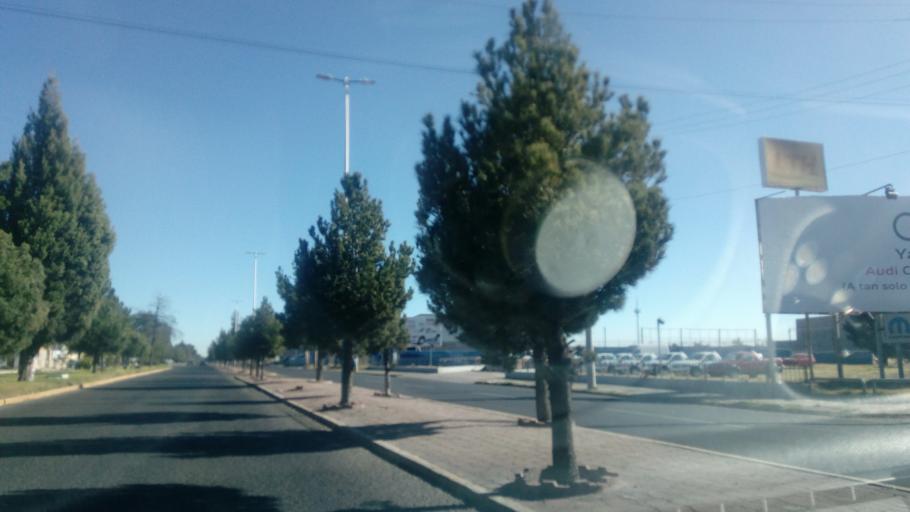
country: MX
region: Durango
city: Victoria de Durango
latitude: 24.0530
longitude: -104.6169
